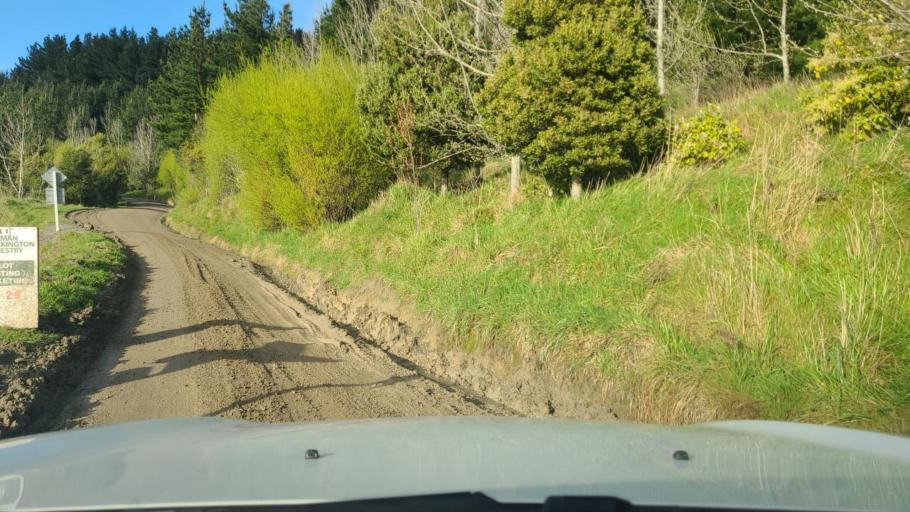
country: NZ
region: Wellington
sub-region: Masterton District
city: Masterton
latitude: -41.1599
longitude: 175.6787
